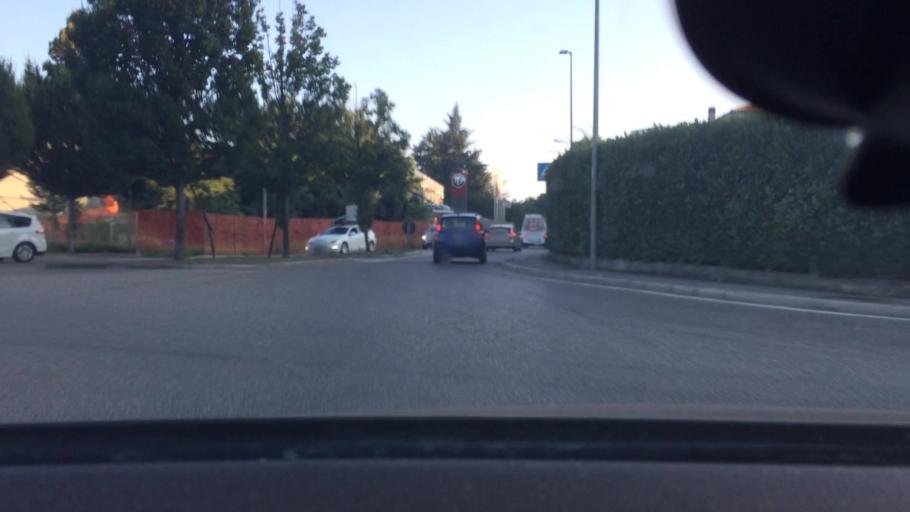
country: IT
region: Lombardy
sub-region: Provincia di Como
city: Grandate
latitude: 45.7784
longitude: 9.0663
